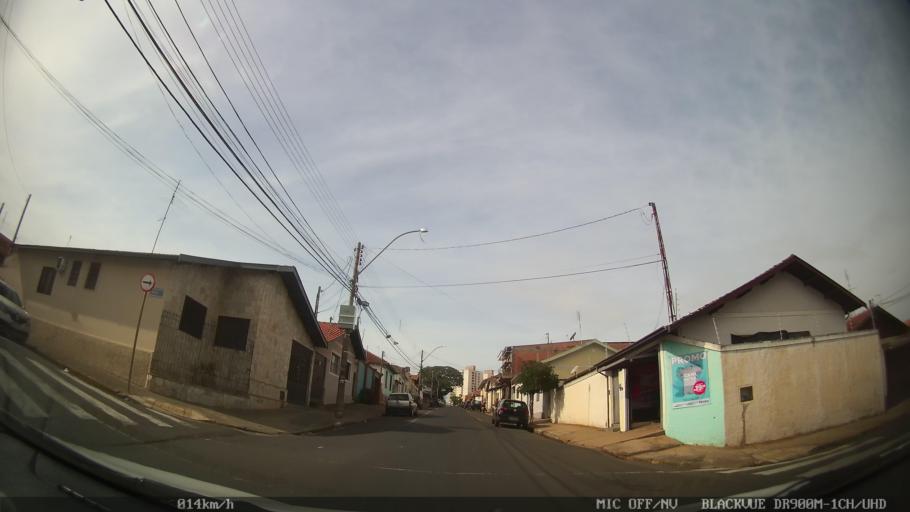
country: BR
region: Sao Paulo
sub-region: Piracicaba
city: Piracicaba
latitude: -22.7395
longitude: -47.6609
